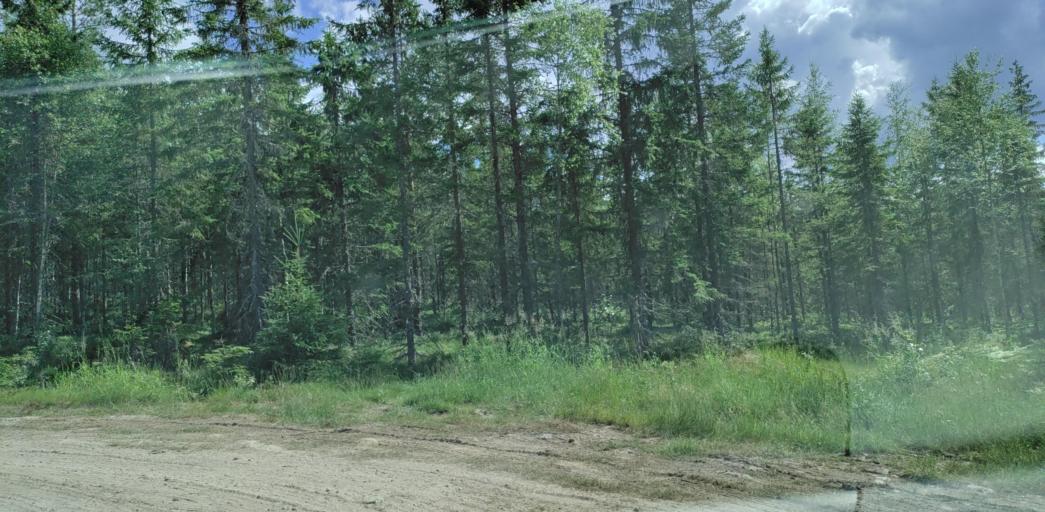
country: SE
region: Vaermland
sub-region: Hagfors Kommun
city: Ekshaerad
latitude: 60.0629
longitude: 13.3386
